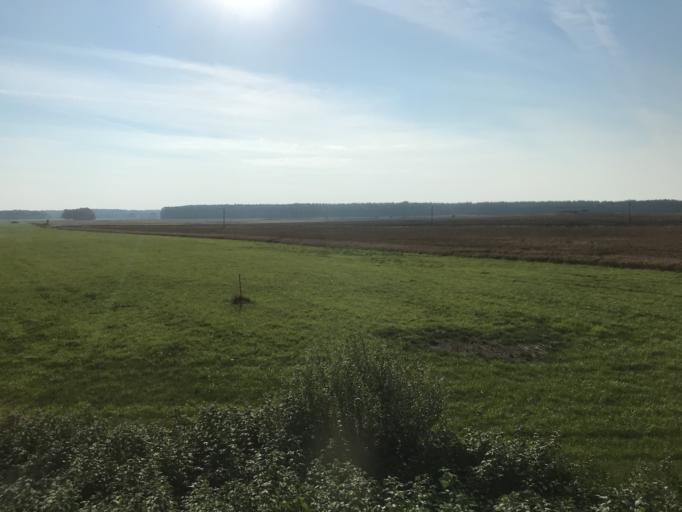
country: CZ
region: Jihocesky
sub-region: Okres Jindrichuv Hradec
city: Lomnice nad Luznici
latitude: 49.0818
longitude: 14.7255
